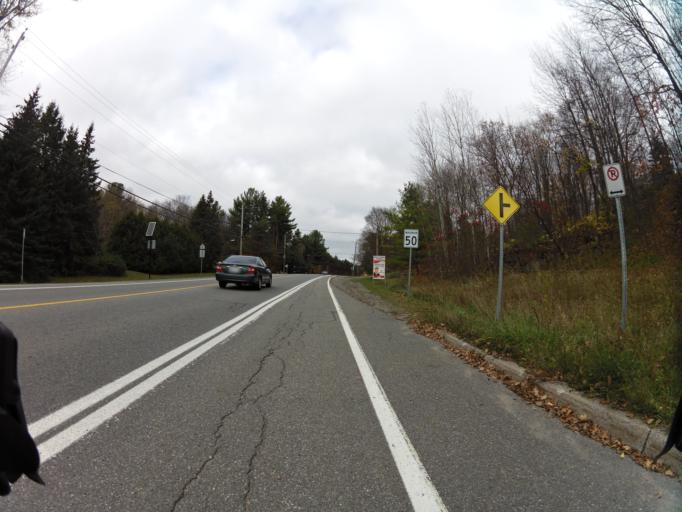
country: CA
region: Quebec
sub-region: Outaouais
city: Gatineau
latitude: 45.5178
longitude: -75.8087
